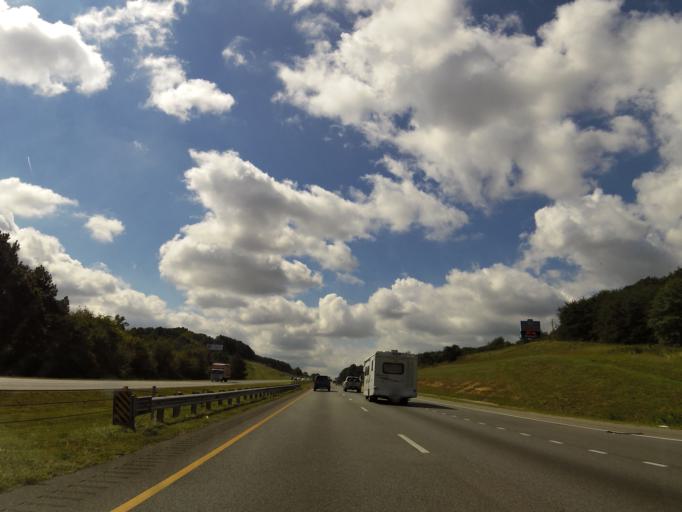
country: US
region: Alabama
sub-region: Jefferson County
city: Bessemer
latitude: 33.3825
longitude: -86.9902
